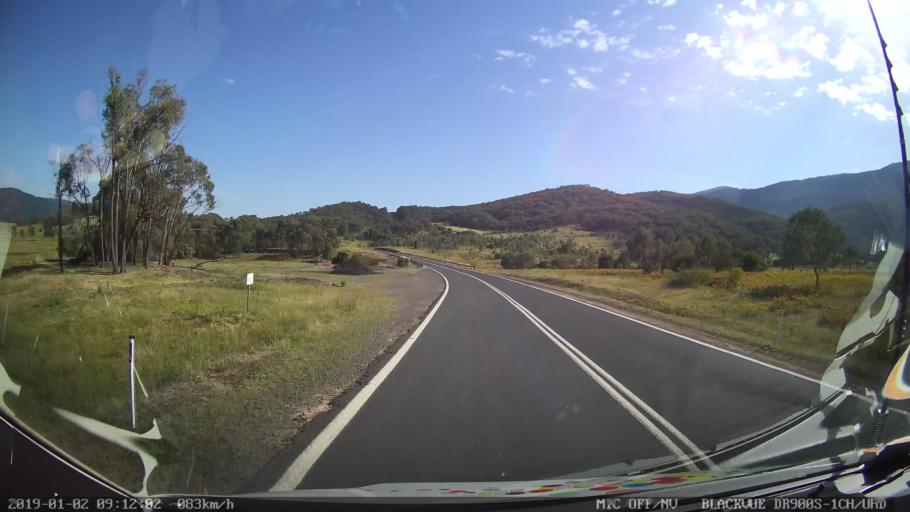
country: AU
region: New South Wales
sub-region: Tumut Shire
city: Tumut
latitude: -35.5054
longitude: 148.2721
